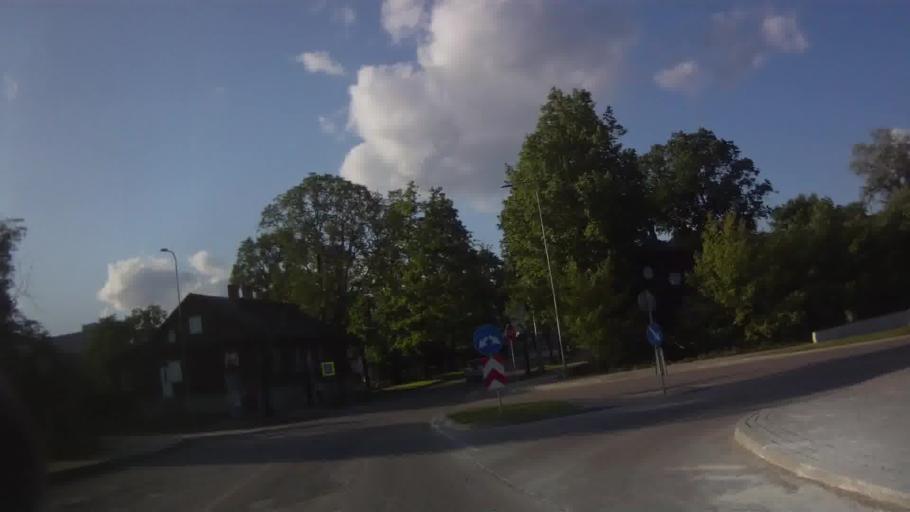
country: LV
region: Rezekne
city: Rezekne
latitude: 56.5029
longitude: 27.3323
